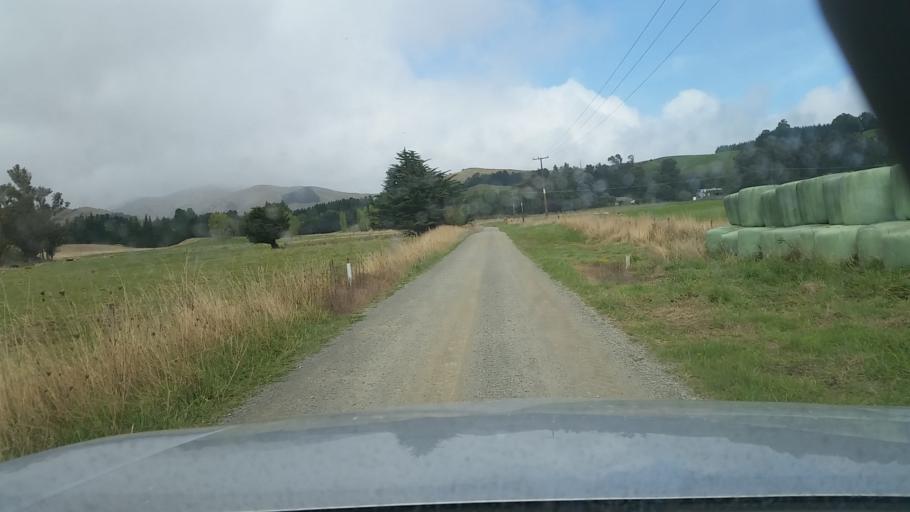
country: NZ
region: Marlborough
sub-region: Marlborough District
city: Blenheim
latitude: -41.7265
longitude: 173.9244
